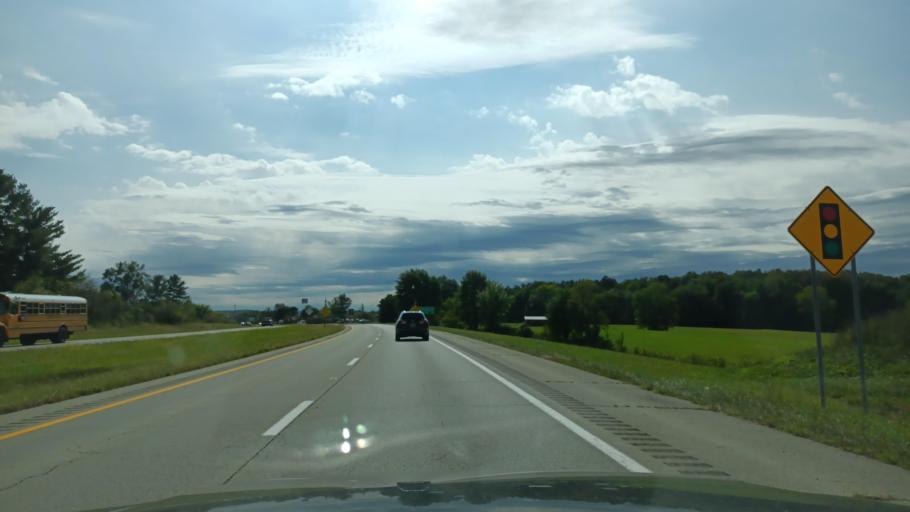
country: US
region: Ohio
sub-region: Athens County
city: Athens
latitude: 39.2387
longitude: -82.1923
